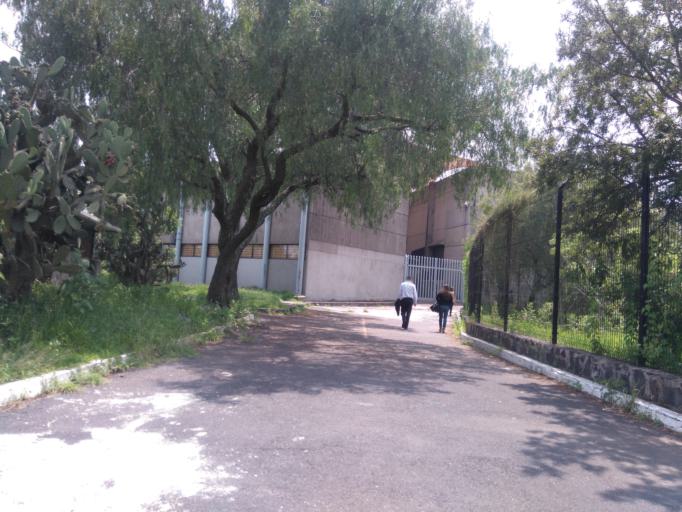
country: MX
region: Mexico City
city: Tlalpan
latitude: 19.3141
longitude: -99.1830
